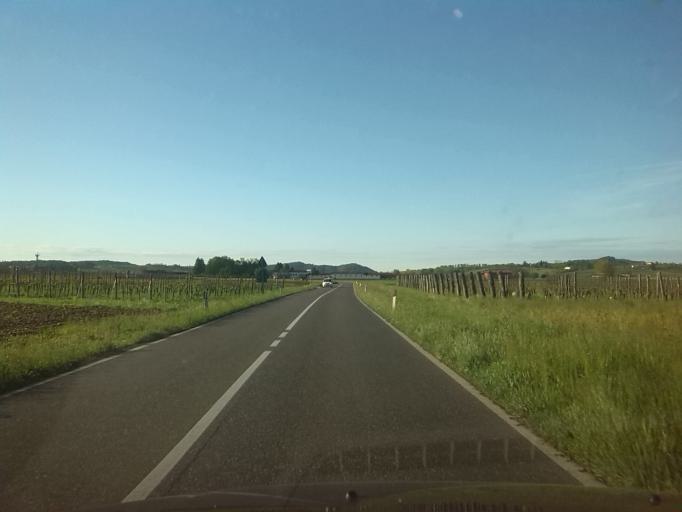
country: IT
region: Friuli Venezia Giulia
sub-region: Provincia di Udine
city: Cividale del Friuli
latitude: 46.0541
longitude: 13.4351
